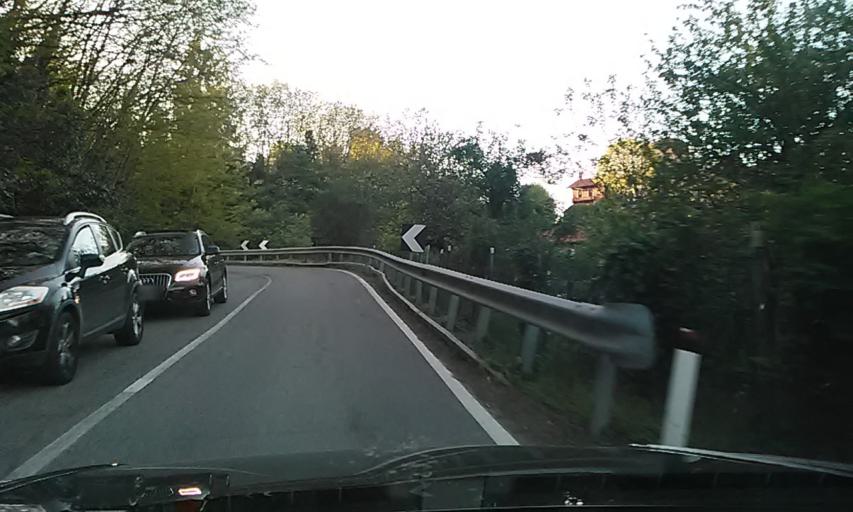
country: IT
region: Piedmont
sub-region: Provincia di Novara
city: Barengo
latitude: 45.5722
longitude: 8.5099
